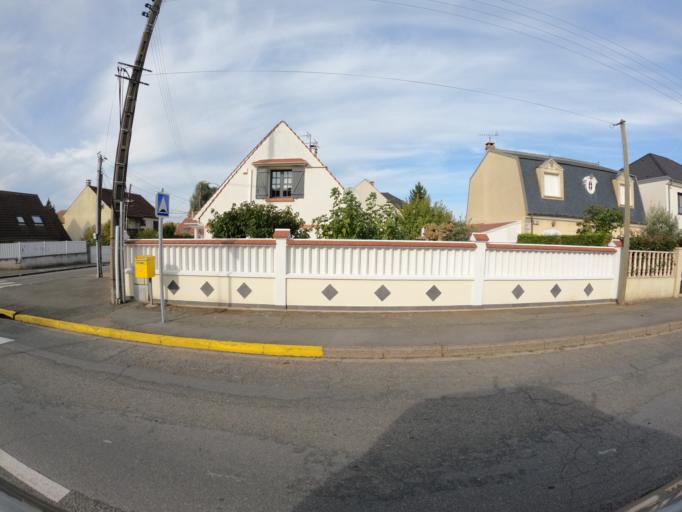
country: FR
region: Ile-de-France
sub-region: Departement de Seine-et-Marne
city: Pontault-Combault
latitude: 48.7894
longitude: 2.6003
